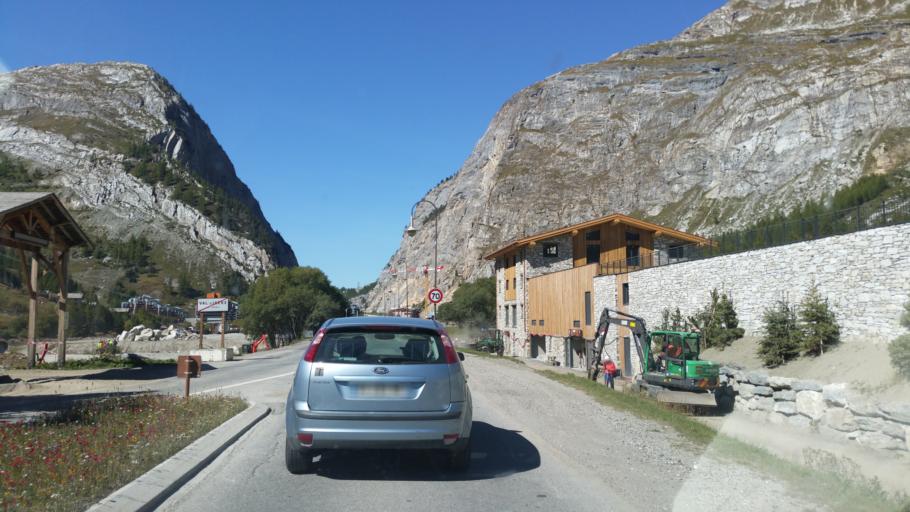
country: FR
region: Rhone-Alpes
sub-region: Departement de la Savoie
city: Val-d'Isere
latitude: 45.4563
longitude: 6.9691
